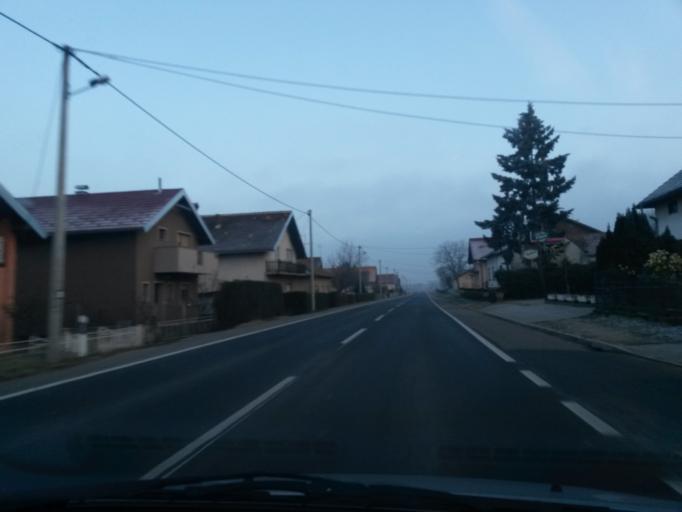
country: HR
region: Varazdinska
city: Ludbreg
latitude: 46.2180
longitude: 16.6850
